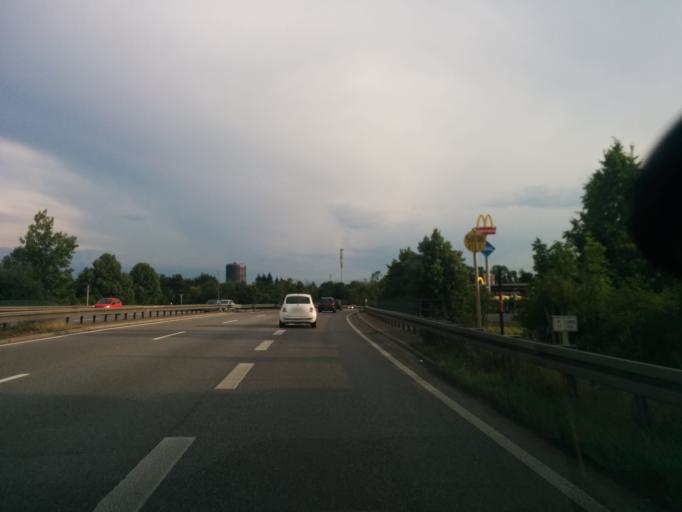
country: DE
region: Bavaria
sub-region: Swabia
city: Gersthofen
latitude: 48.3995
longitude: 10.8698
